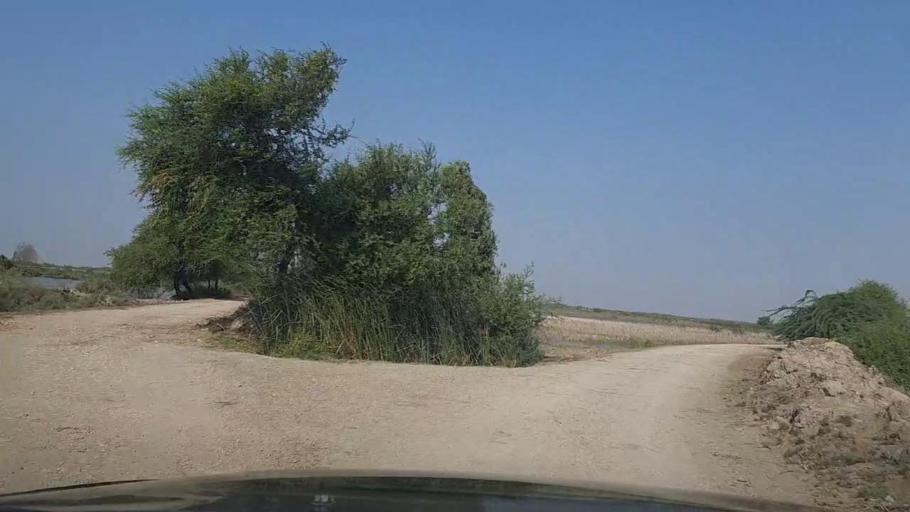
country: PK
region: Sindh
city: Thatta
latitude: 24.6374
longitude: 67.8135
